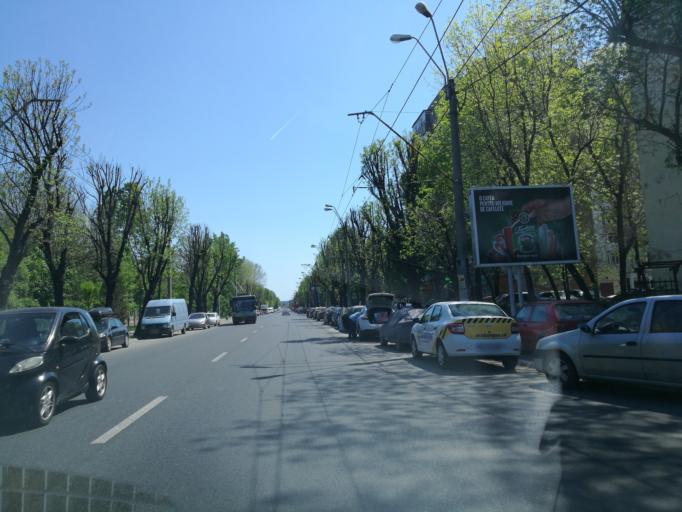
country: RO
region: Ilfov
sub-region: Comuna Popesti-Leordeni
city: Popesti-Leordeni
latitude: 44.3857
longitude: 26.1215
